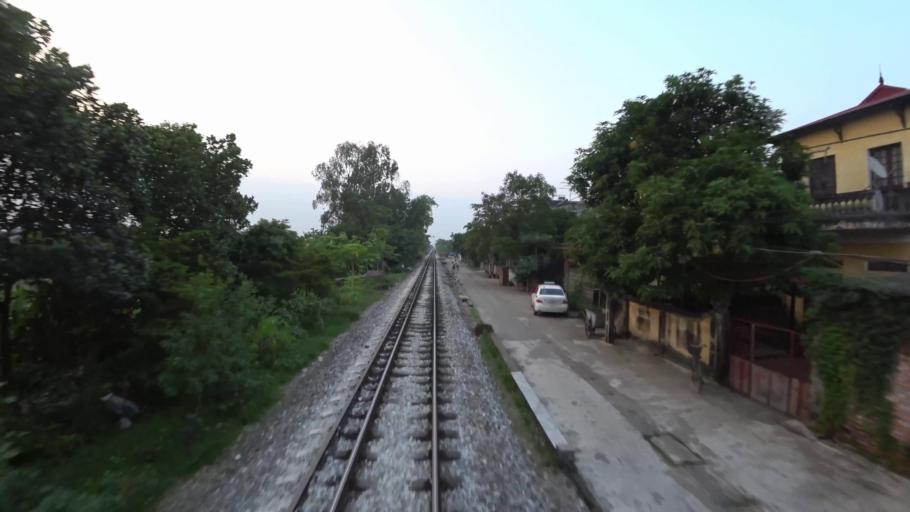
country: VN
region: Ha Noi
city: Dong Anh
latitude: 21.1429
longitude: 105.8635
